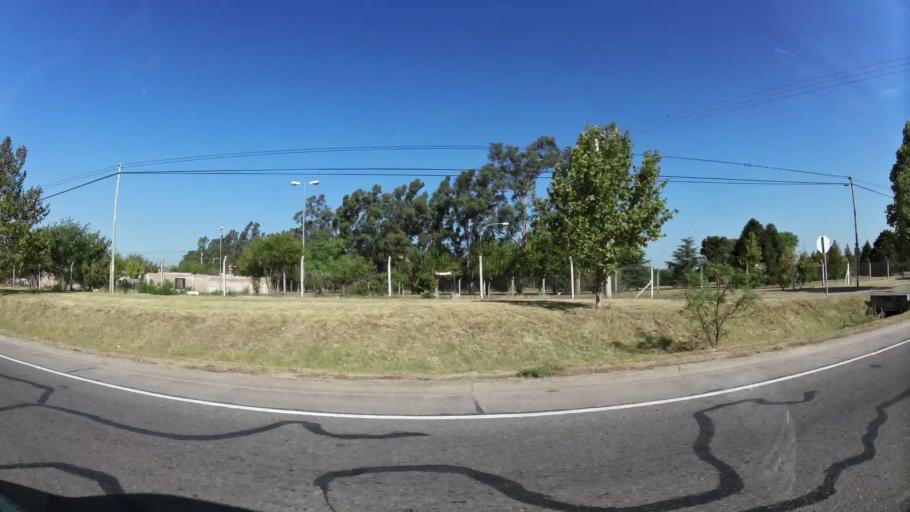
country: AR
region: Cordoba
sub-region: Departamento de Capital
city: Cordoba
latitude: -31.4841
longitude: -64.2443
